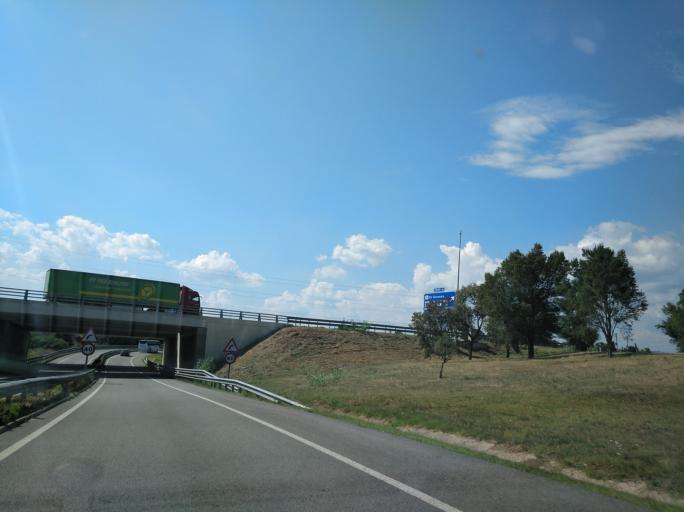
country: ES
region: Catalonia
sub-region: Provincia de Girona
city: Riudellots de la Selva
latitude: 41.8960
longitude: 2.7760
